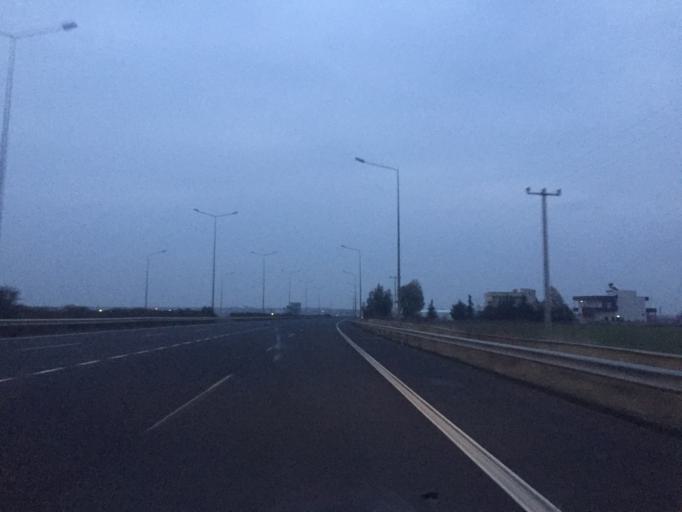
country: TR
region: Sanliurfa
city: Camlidere
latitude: 37.1607
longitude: 39.0197
